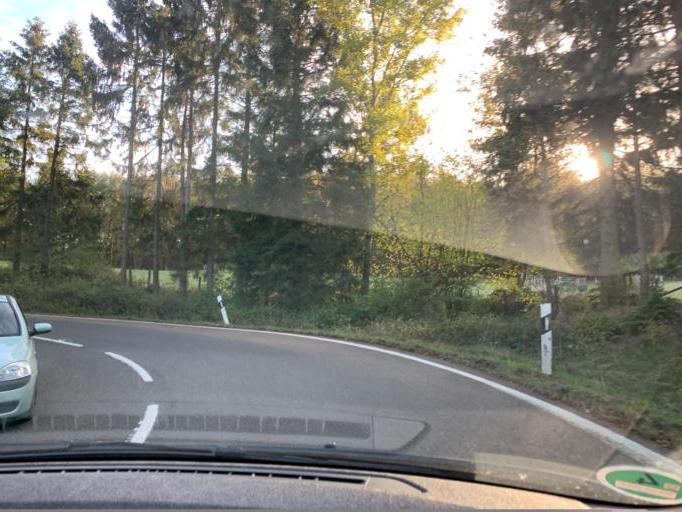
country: DE
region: North Rhine-Westphalia
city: Heimbach
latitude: 50.6122
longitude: 6.4802
